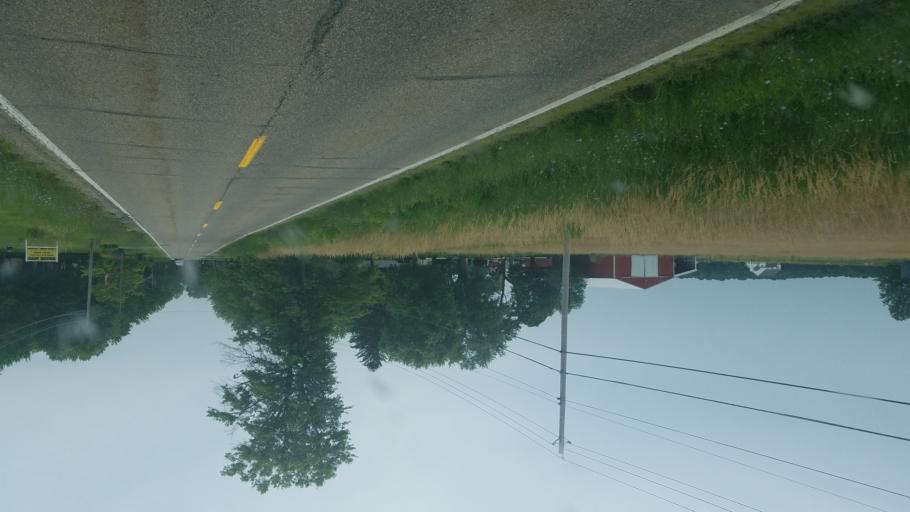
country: US
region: Ohio
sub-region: Portage County
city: Ravenna
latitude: 41.0994
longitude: -81.1577
